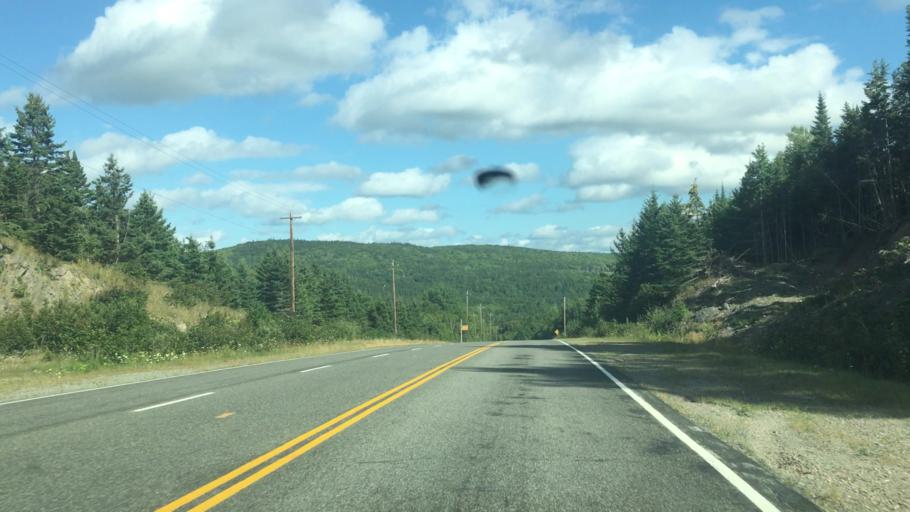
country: CA
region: Nova Scotia
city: Sydney
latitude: 45.8143
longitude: -60.6823
